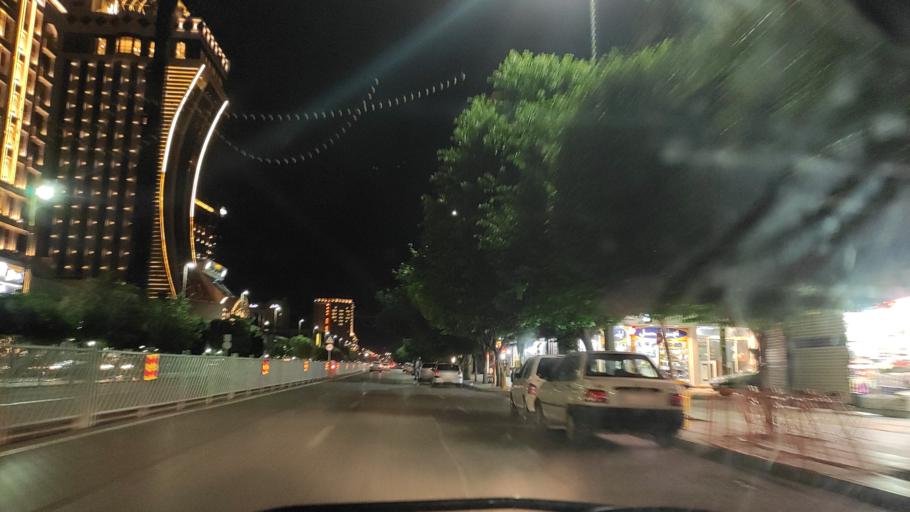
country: IR
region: Razavi Khorasan
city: Mashhad
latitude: 36.2780
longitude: 59.6070
